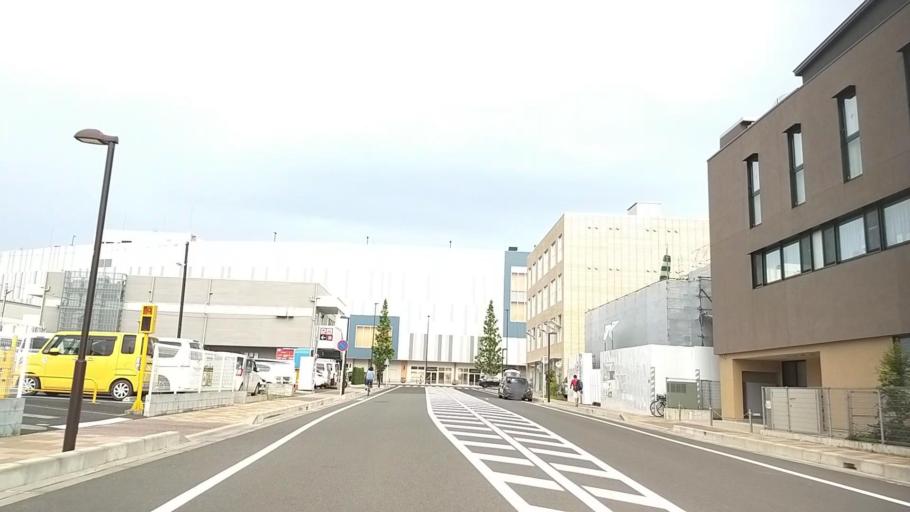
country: JP
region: Kanagawa
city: Atsugi
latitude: 35.4560
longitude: 139.3873
